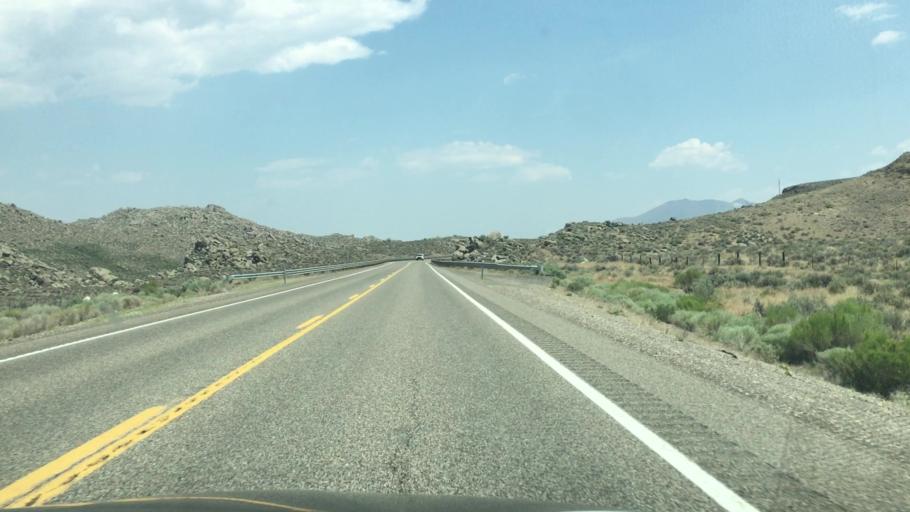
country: US
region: Nevada
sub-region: Elko County
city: Jackpot
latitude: 41.7341
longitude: -114.7894
